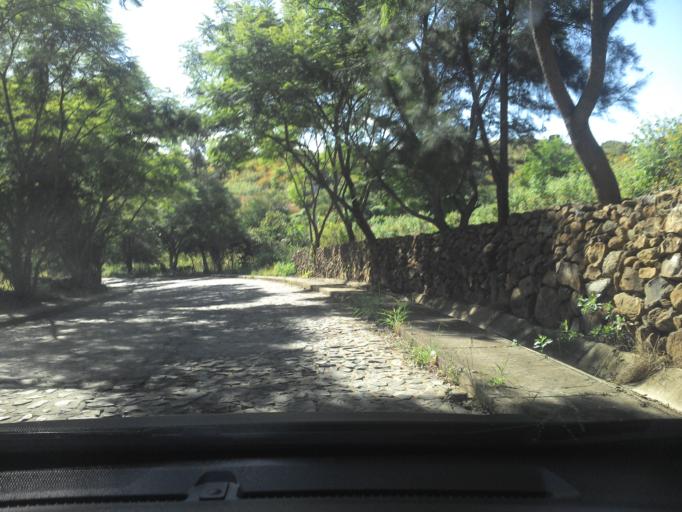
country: MX
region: Jalisco
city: Teuchitlan
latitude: 20.6931
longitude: -103.8428
